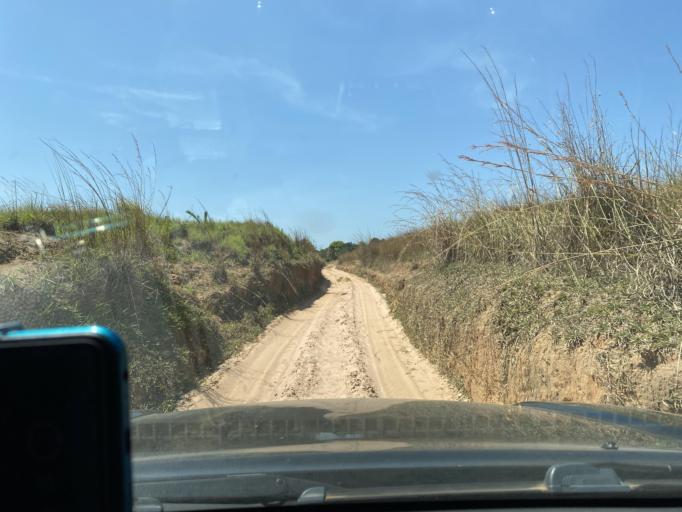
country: CD
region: Kasai-Oriental
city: Kabinda
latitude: -5.9193
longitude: 24.8453
